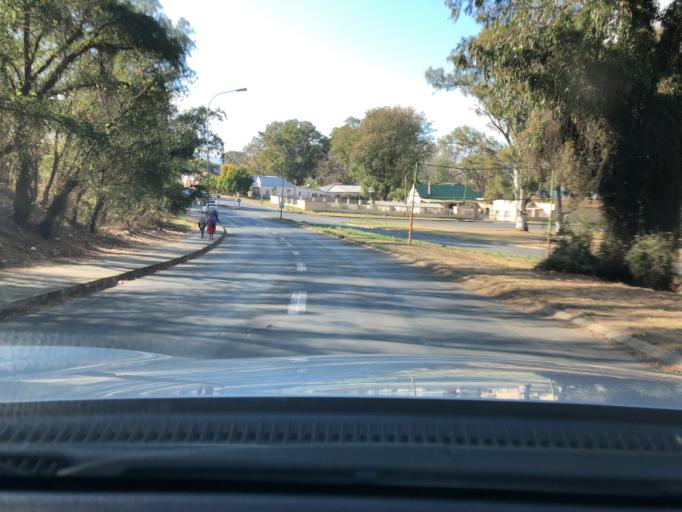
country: ZA
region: KwaZulu-Natal
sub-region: uThukela District Municipality
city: Ladysmith
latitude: -28.5588
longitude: 29.7744
